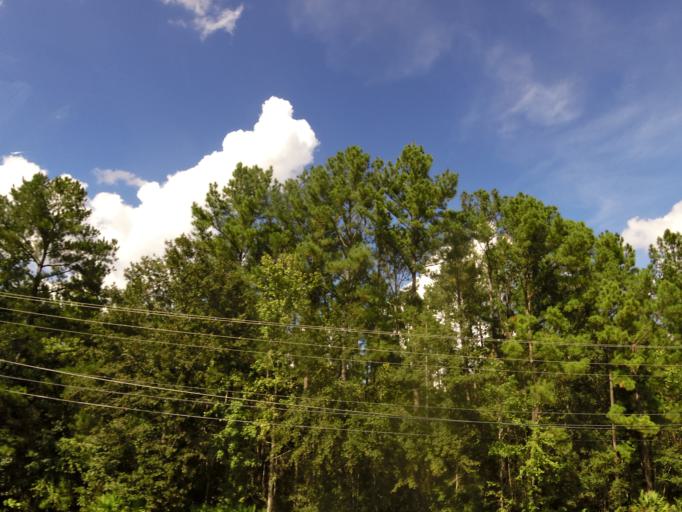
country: US
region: Georgia
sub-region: Echols County
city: Statenville
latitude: 30.7042
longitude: -83.0344
